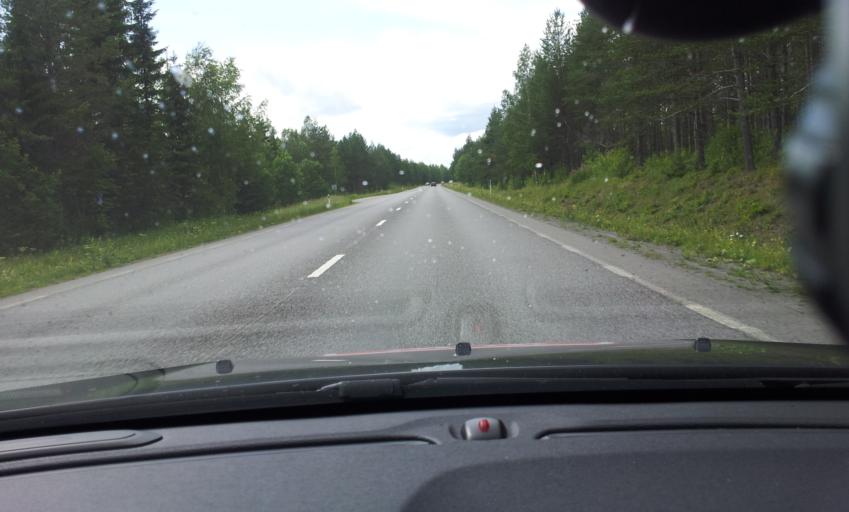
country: SE
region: Jaemtland
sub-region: Krokoms Kommun
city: Krokom
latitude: 63.3136
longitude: 14.1139
